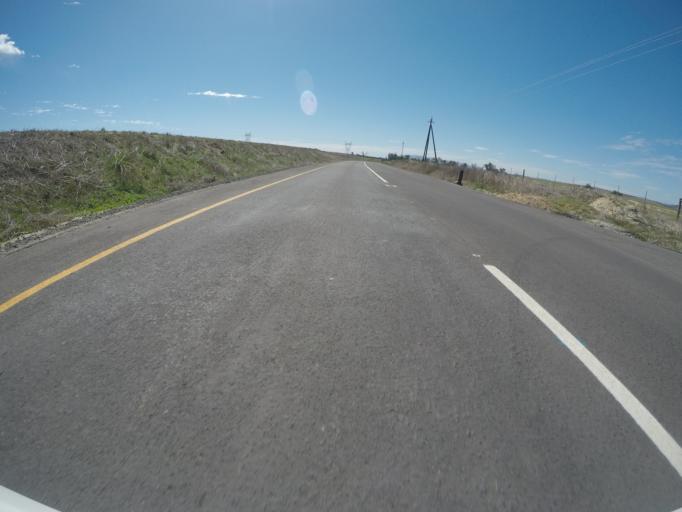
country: ZA
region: Western Cape
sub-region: West Coast District Municipality
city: Malmesbury
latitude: -33.5161
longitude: 18.6547
